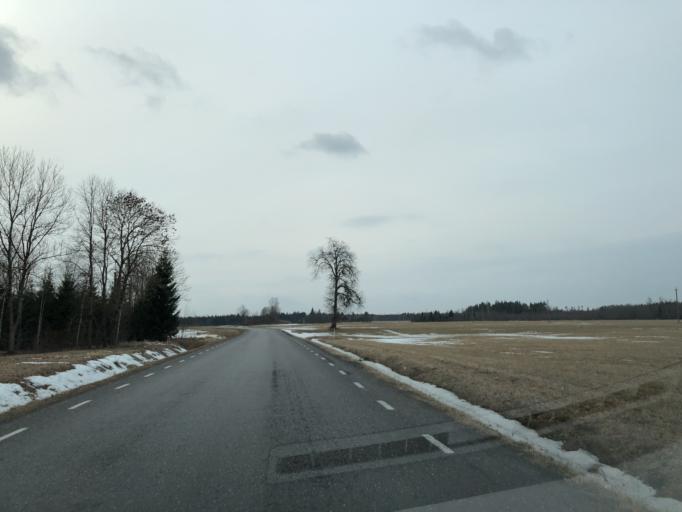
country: EE
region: Paernumaa
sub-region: Vaendra vald (alev)
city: Vandra
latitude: 58.6807
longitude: 25.0026
